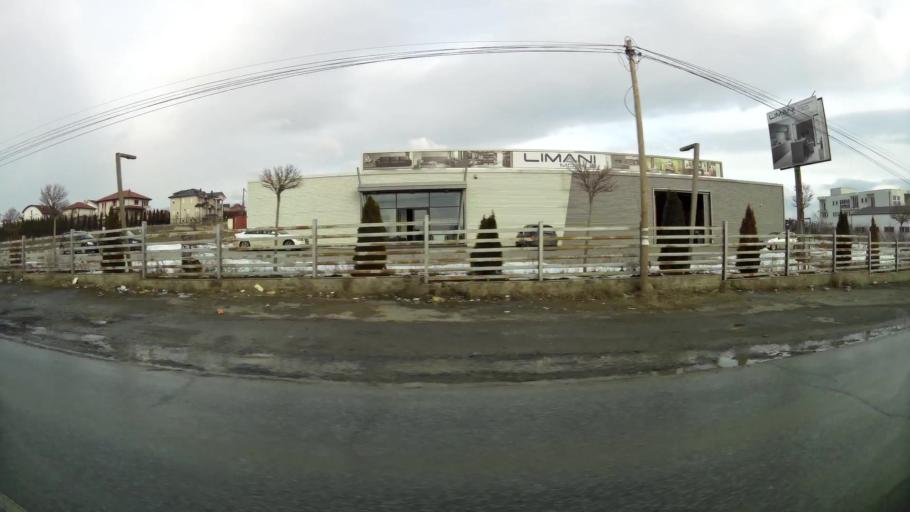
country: XK
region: Pristina
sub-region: Komuna e Prishtines
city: Pristina
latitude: 42.6238
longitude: 21.1612
